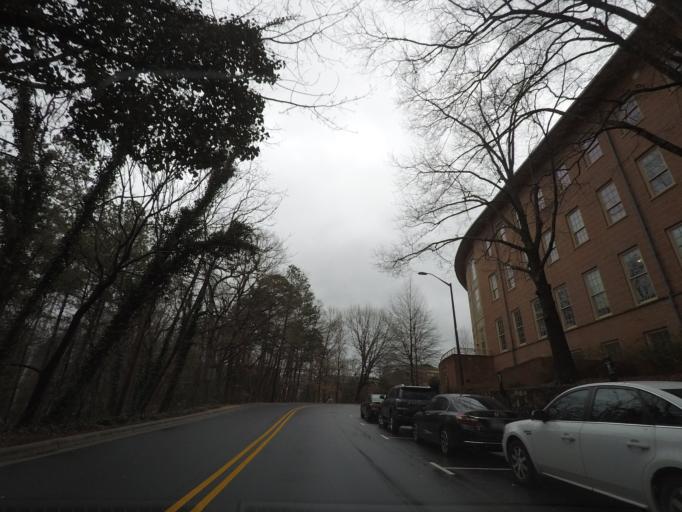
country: US
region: North Carolina
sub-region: Orange County
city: Chapel Hill
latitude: 35.9049
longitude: -79.0449
